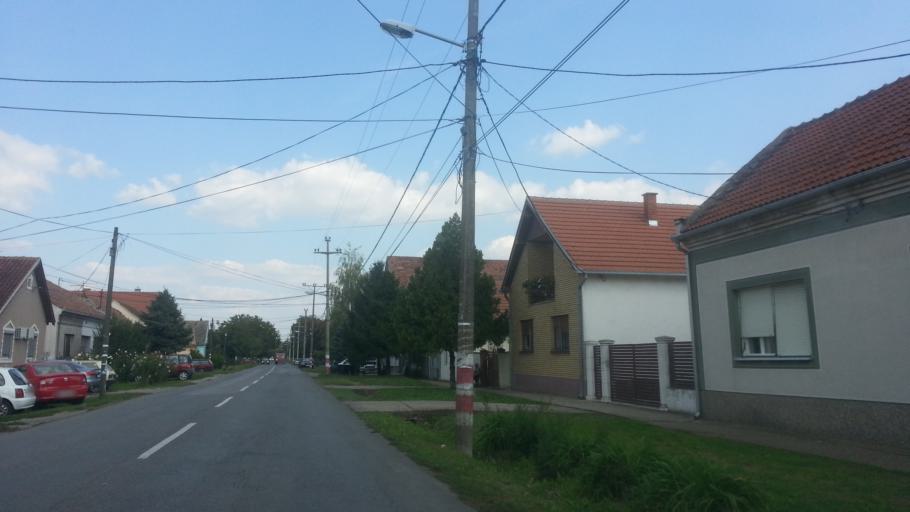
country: RS
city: Novi Banovci
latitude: 44.9092
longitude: 20.2787
